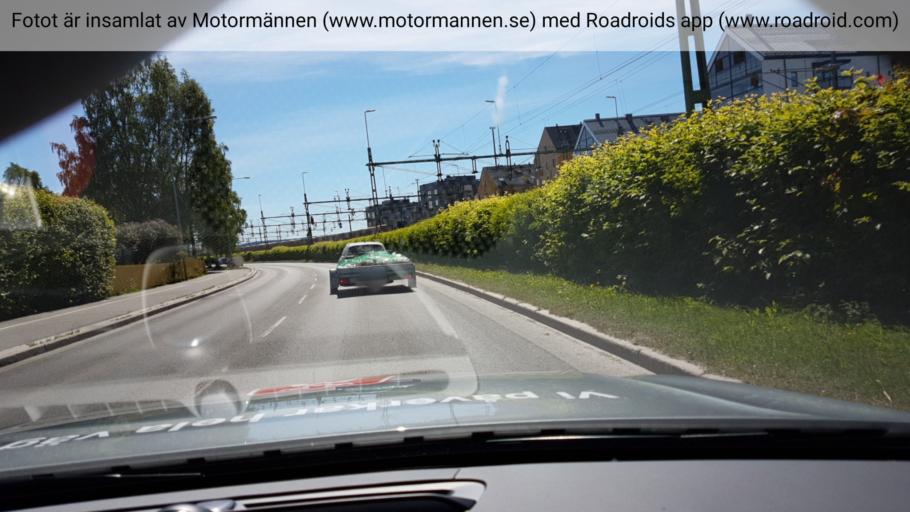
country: SE
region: Jaemtland
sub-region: OEstersunds Kommun
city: Ostersund
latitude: 63.1746
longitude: 14.6322
